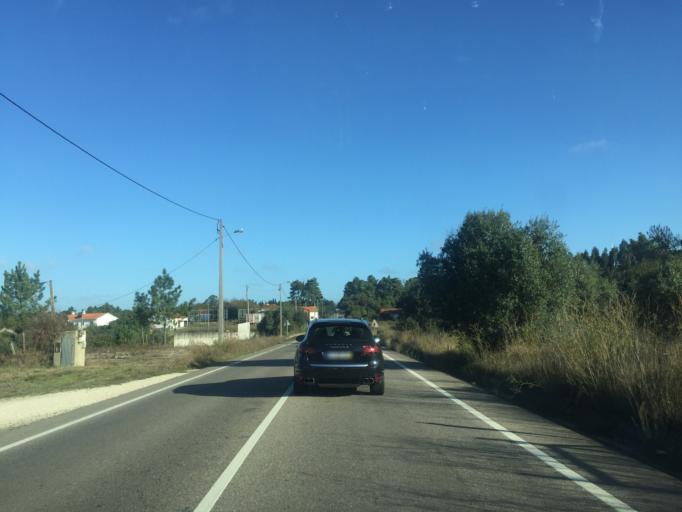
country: PT
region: Leiria
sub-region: Alcobaca
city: Benedita
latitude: 39.3858
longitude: -8.9610
